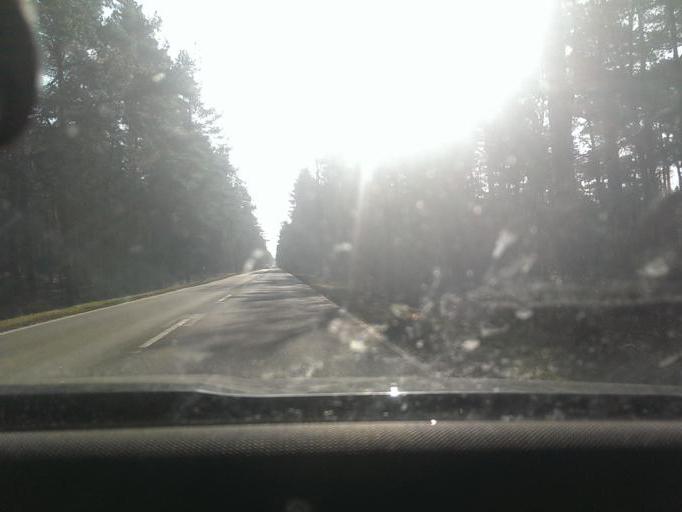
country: DE
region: Lower Saxony
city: Lindwedel
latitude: 52.6297
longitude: 9.6950
